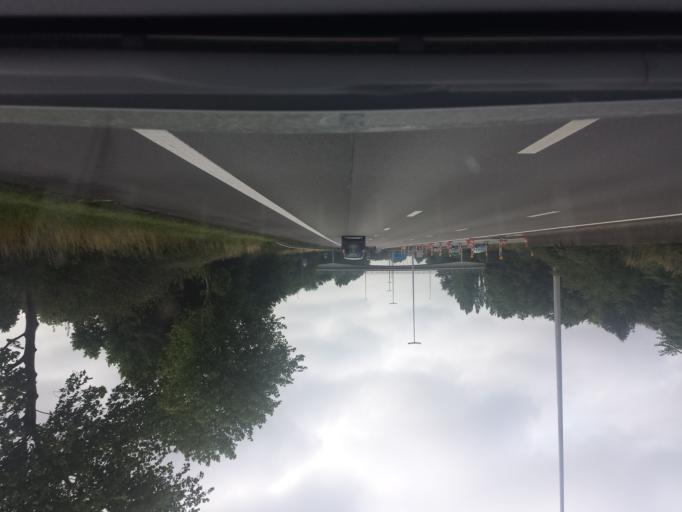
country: BE
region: Flanders
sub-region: Provincie West-Vlaanderen
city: Waregem
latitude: 50.8769
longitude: 3.4539
